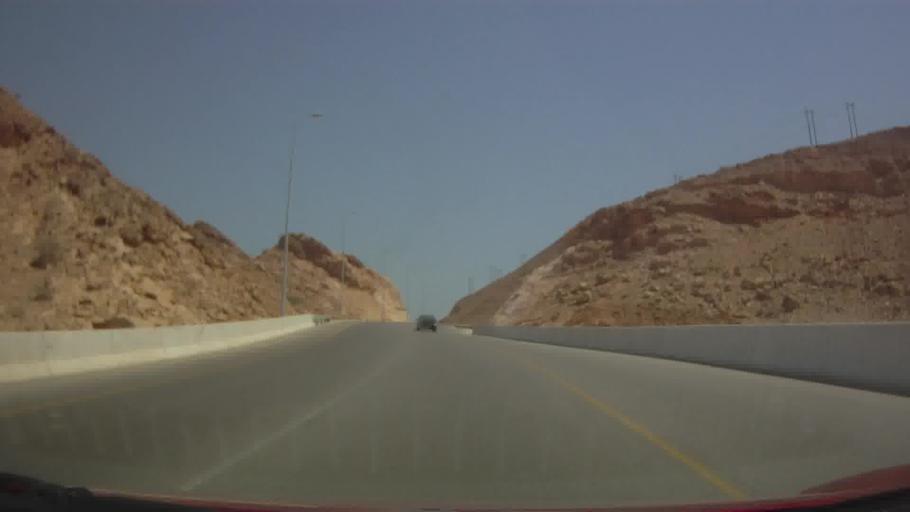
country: OM
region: Muhafazat Masqat
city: Muscat
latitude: 23.5405
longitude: 58.6350
